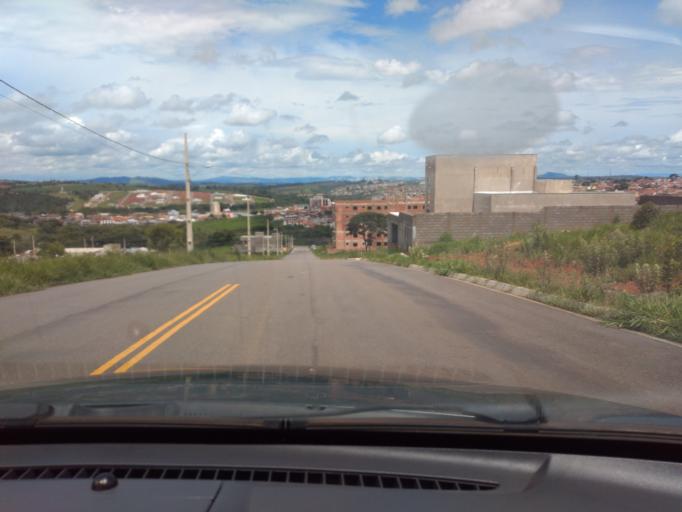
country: BR
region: Minas Gerais
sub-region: Tres Coracoes
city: Tres Coracoes
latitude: -21.6786
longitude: -45.2780
